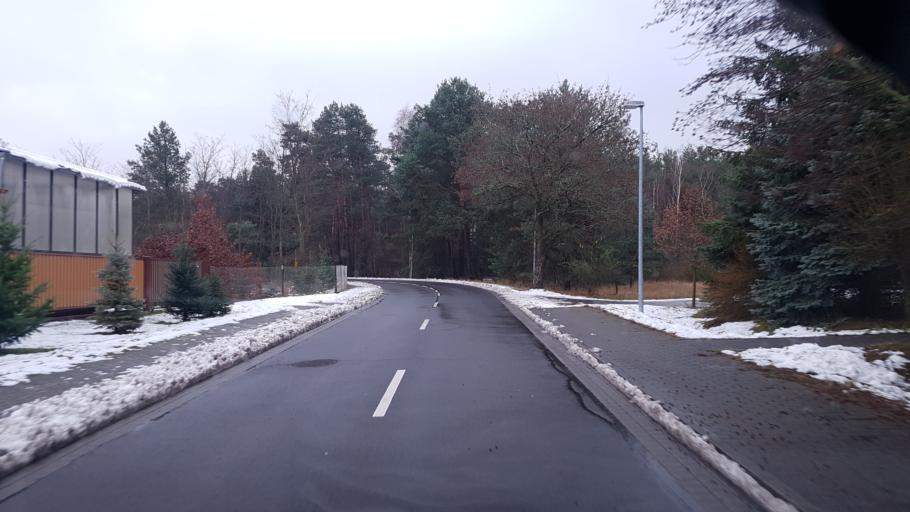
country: DE
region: Brandenburg
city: Schenkendobern
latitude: 51.9086
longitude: 14.6273
